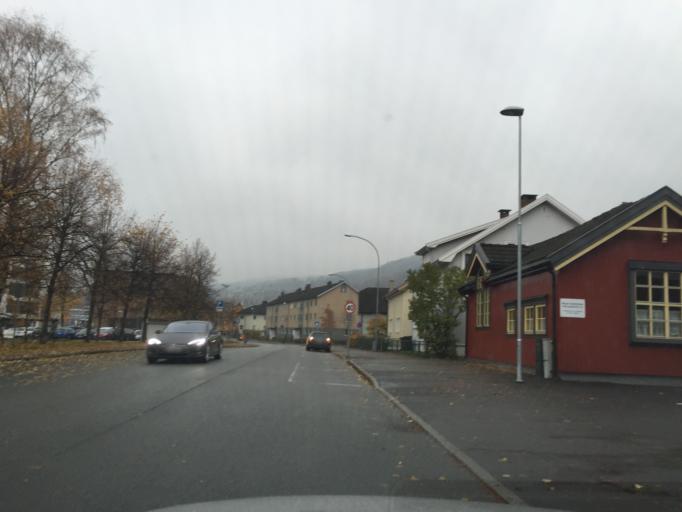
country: NO
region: Buskerud
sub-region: Drammen
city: Drammen
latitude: 59.7378
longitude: 10.1965
